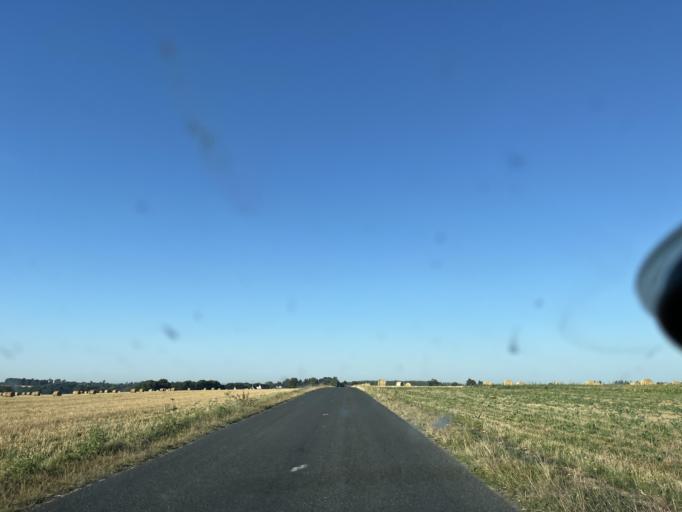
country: FR
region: Haute-Normandie
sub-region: Departement de la Seine-Maritime
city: Lillebonne
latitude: 49.5510
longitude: 0.5680
